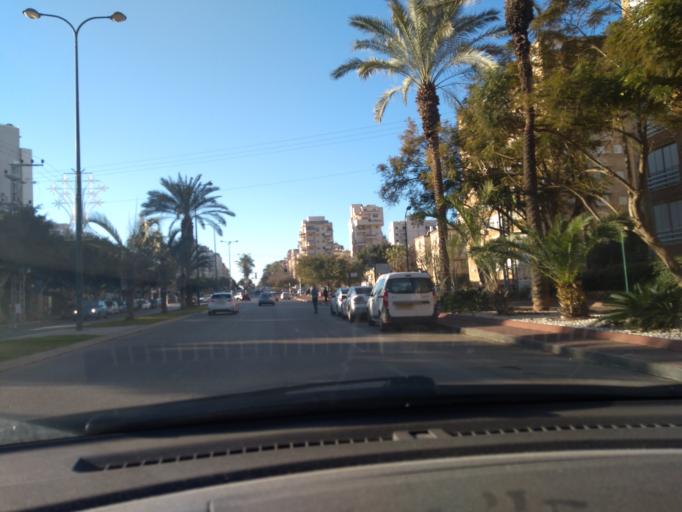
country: IL
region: Central District
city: Netanya
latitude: 32.3393
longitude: 34.8599
